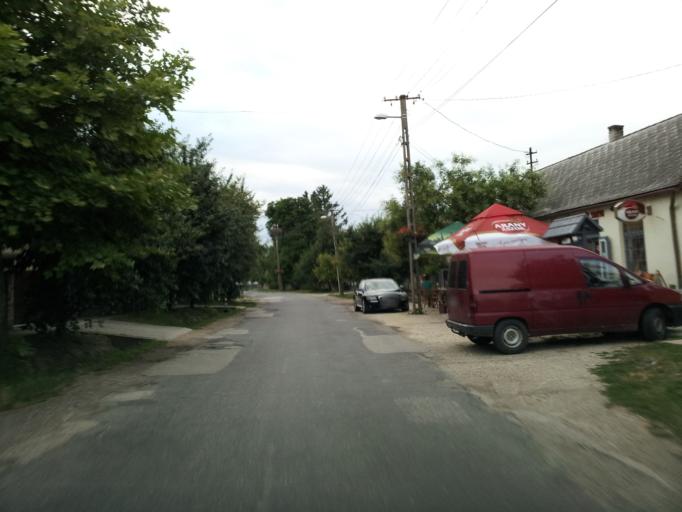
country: HU
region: Somogy
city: Balatonszabadi
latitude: 46.8843
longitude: 18.1501
